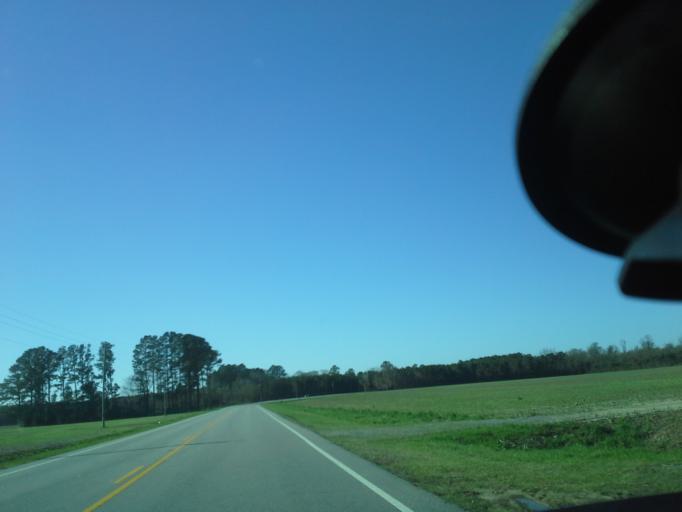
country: US
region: North Carolina
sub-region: Beaufort County
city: Belhaven
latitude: 35.5276
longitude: -76.7640
